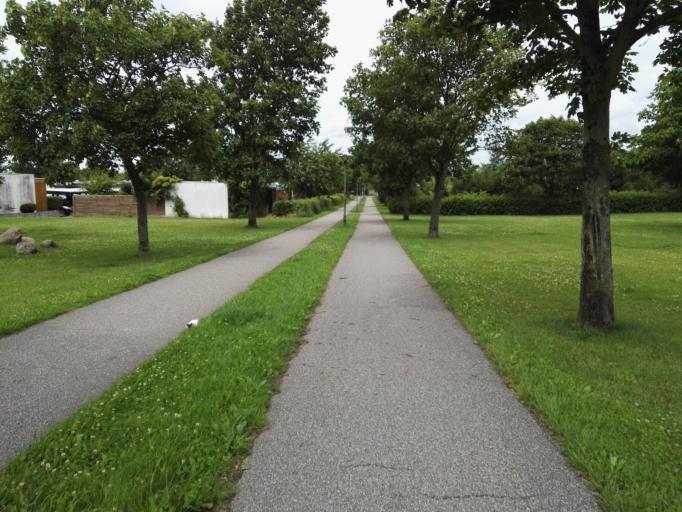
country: DK
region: Capital Region
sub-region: Egedal Kommune
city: Olstykke
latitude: 55.7777
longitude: 12.1647
